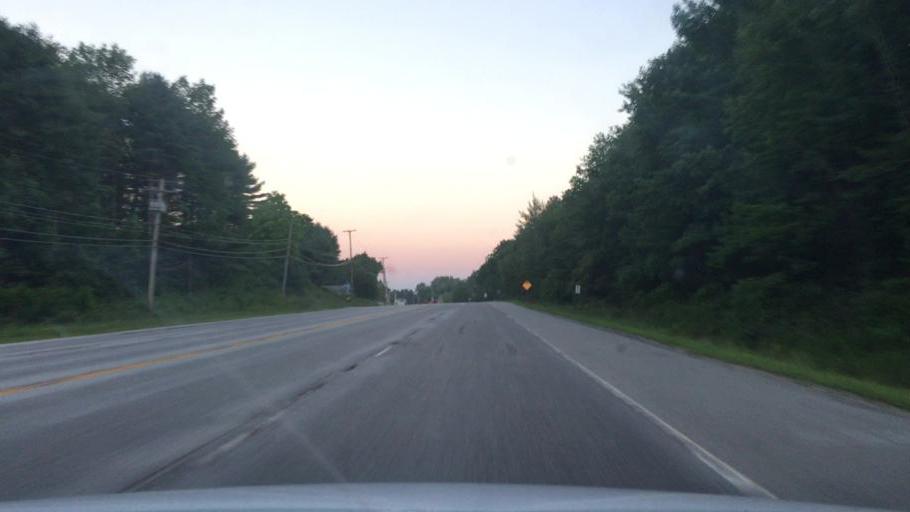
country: US
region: Maine
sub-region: Androscoggin County
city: Auburn
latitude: 44.1505
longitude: -70.2311
